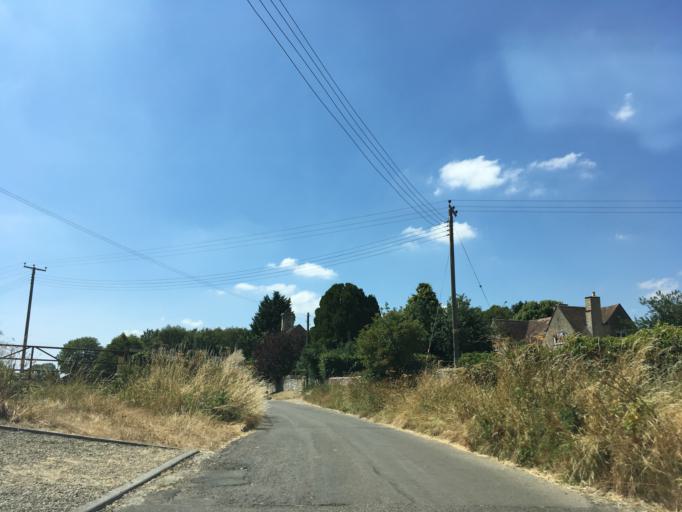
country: GB
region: England
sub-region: Gloucestershire
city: Coates
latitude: 51.6807
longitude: -2.0858
